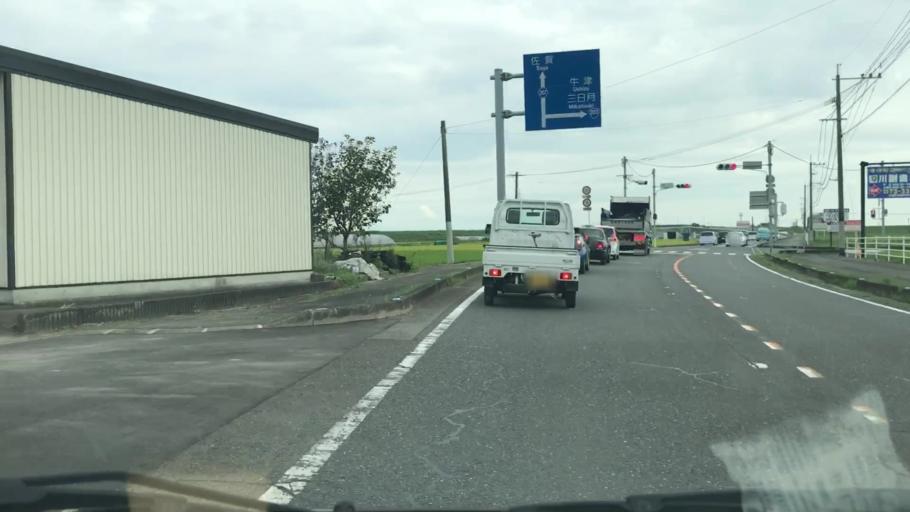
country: JP
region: Saga Prefecture
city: Saga-shi
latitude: 33.2852
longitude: 130.2514
